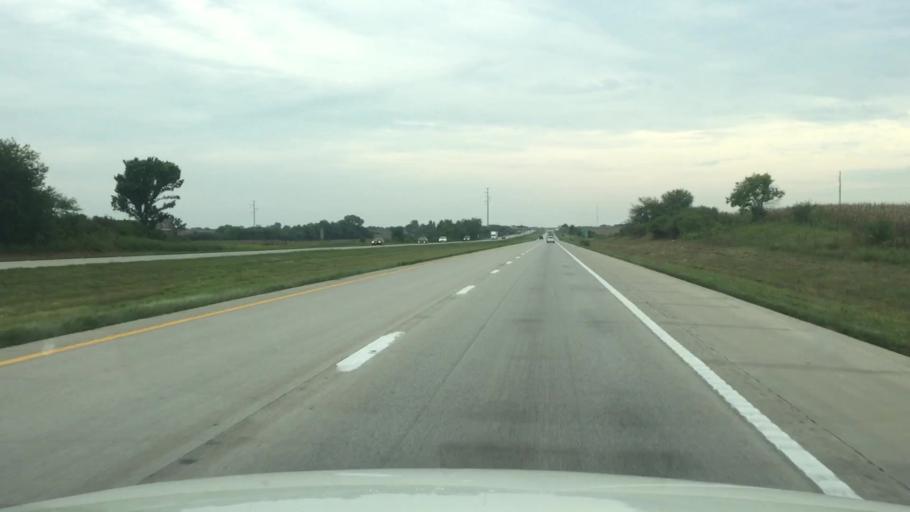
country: US
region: Missouri
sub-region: Clinton County
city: Cameron
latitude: 39.6431
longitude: -94.2421
